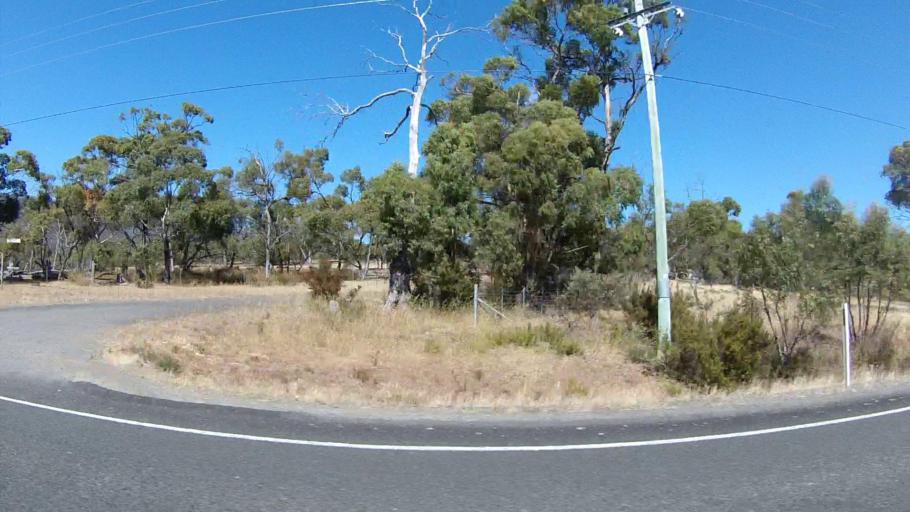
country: AU
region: Tasmania
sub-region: Sorell
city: Sorell
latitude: -42.5825
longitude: 147.8111
